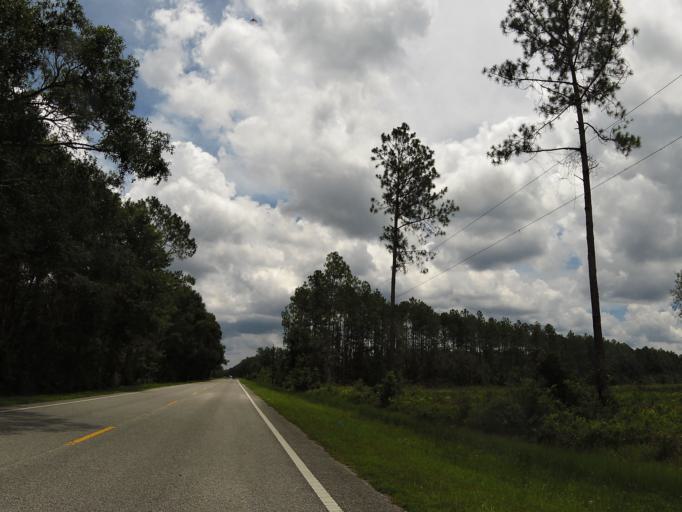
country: US
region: Florida
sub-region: Saint Johns County
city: Saint Augustine Shores
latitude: 29.6586
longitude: -81.4082
